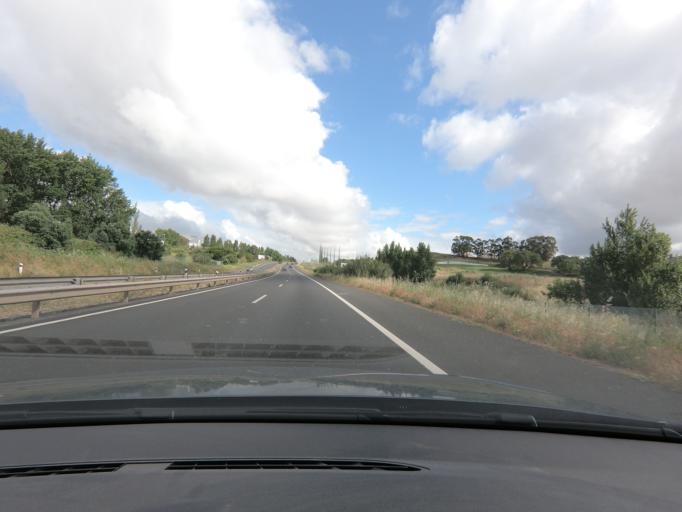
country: PT
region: Lisbon
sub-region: Oeiras
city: Barcarena
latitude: 38.7423
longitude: -9.3003
